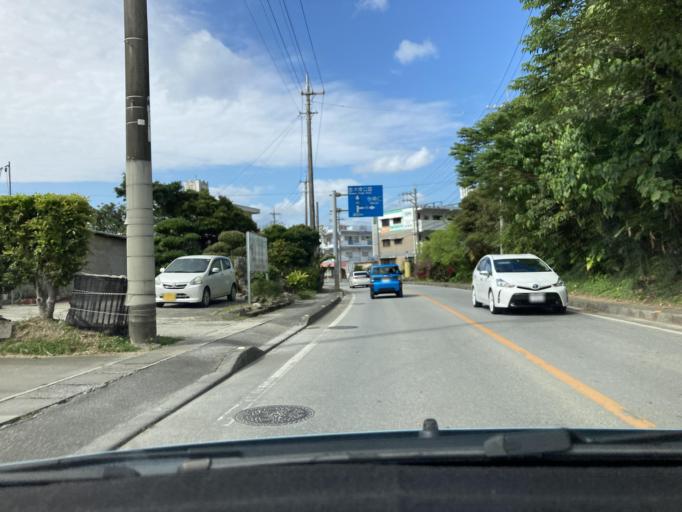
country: JP
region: Okinawa
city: Nago
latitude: 26.6572
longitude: 127.9034
